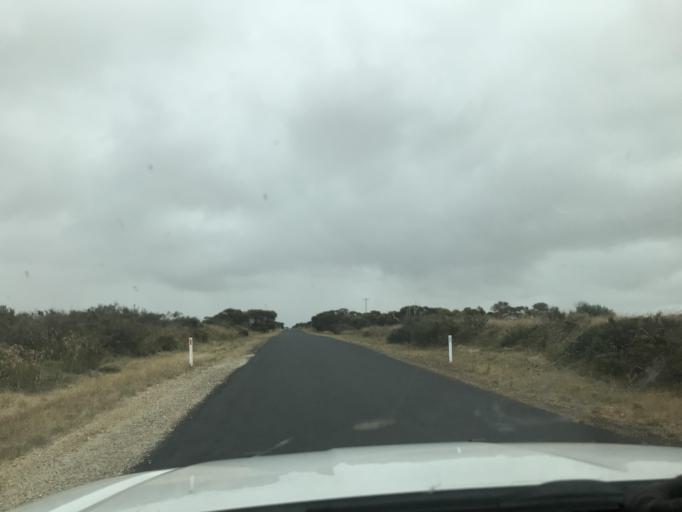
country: AU
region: South Australia
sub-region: Tatiara
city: Bordertown
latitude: -36.1173
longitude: 141.0381
